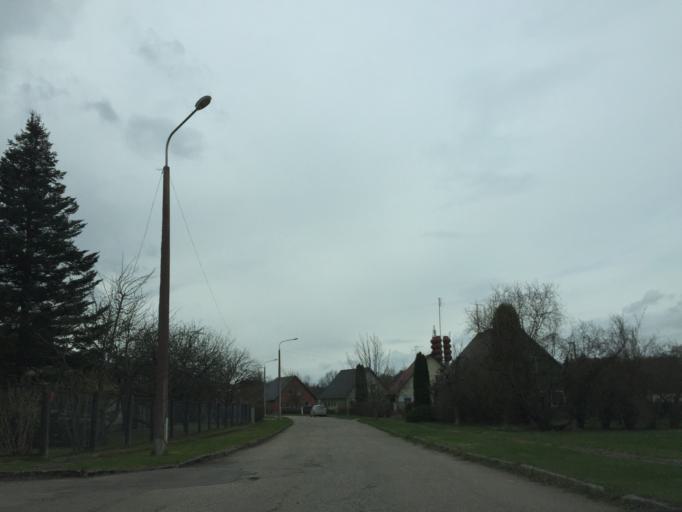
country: LV
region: Priekuli
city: Priekuli
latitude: 57.3499
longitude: 25.3308
